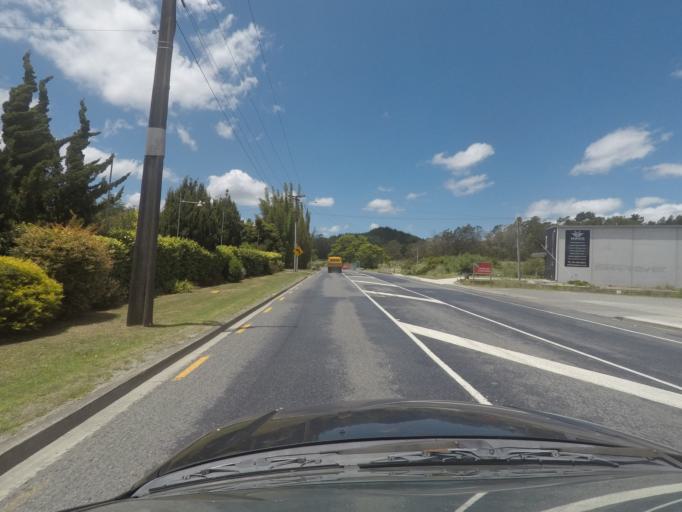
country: NZ
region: Northland
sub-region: Whangarei
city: Whangarei
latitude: -35.7521
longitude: 174.3179
